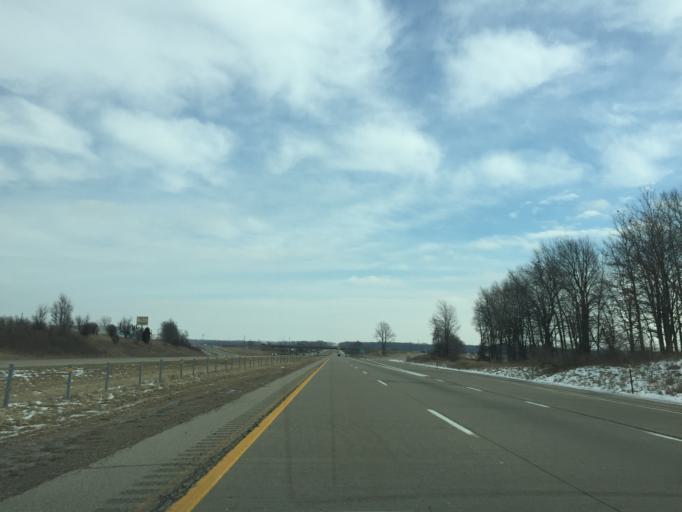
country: US
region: Michigan
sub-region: Ionia County
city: Saranac
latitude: 42.8793
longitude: -85.2505
